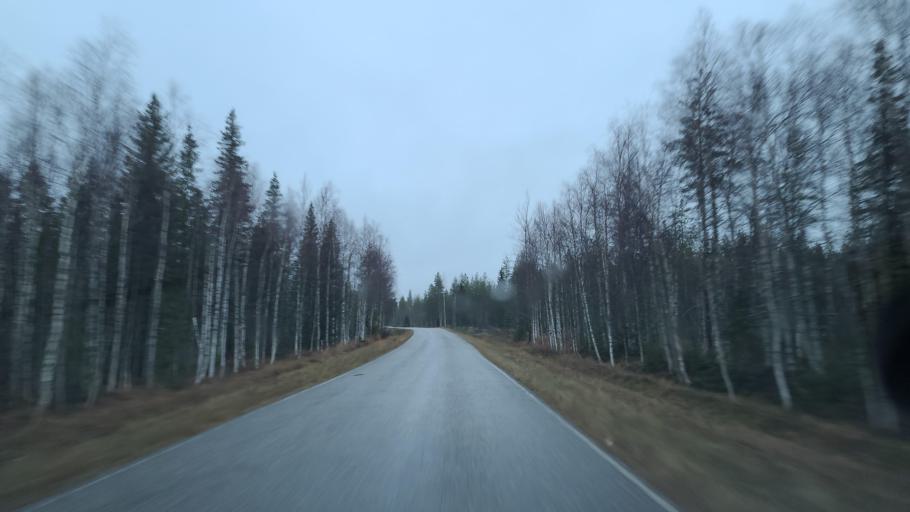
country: FI
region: Lapland
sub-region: Kemi-Tornio
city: Simo
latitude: 65.9240
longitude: 25.2019
